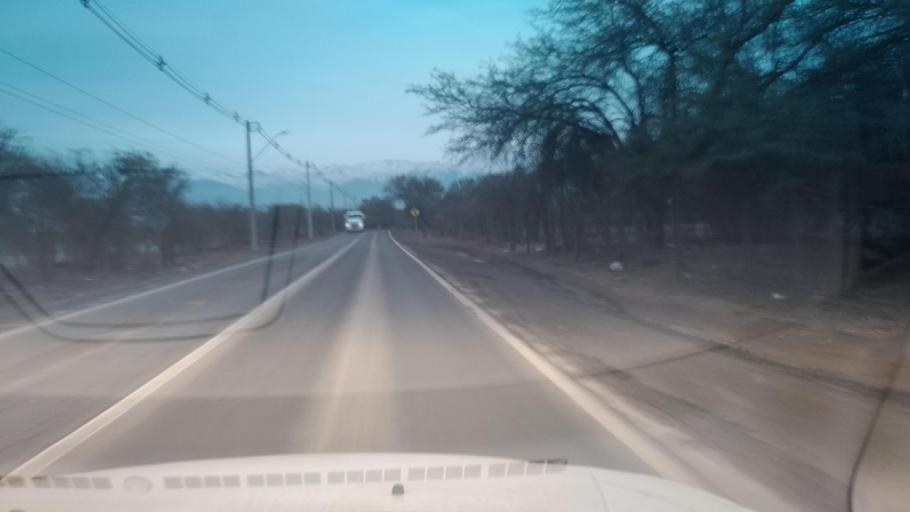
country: CL
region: Santiago Metropolitan
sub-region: Provincia de Chacabuco
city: Chicureo Abajo
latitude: -33.0918
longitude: -70.7380
